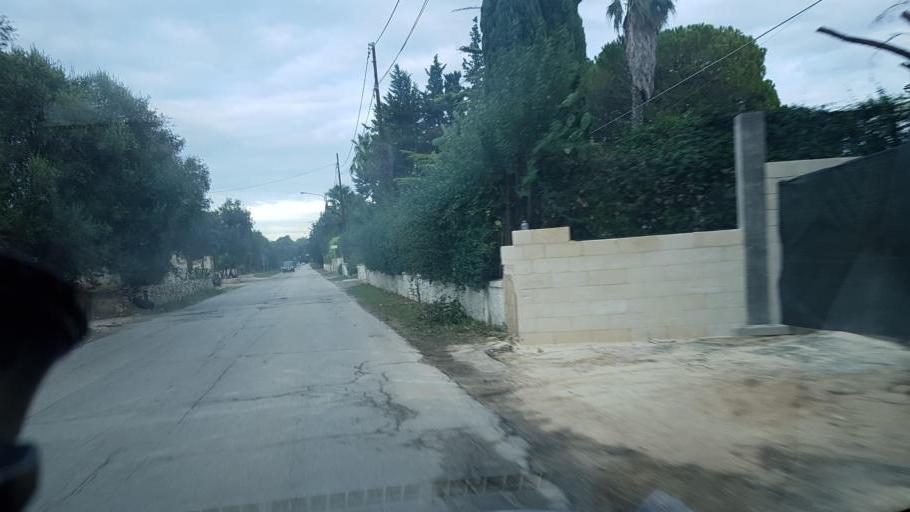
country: IT
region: Apulia
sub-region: Provincia di Brindisi
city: Latiano
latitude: 40.5444
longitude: 17.7018
